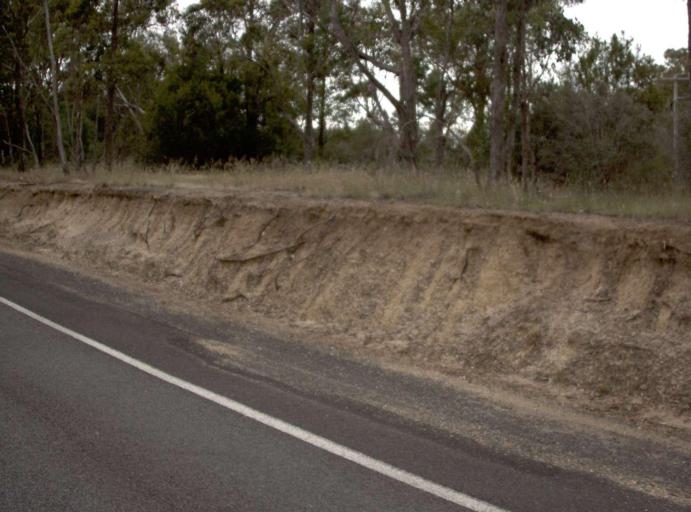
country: AU
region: Victoria
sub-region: Wellington
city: Sale
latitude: -38.4345
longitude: 146.9500
